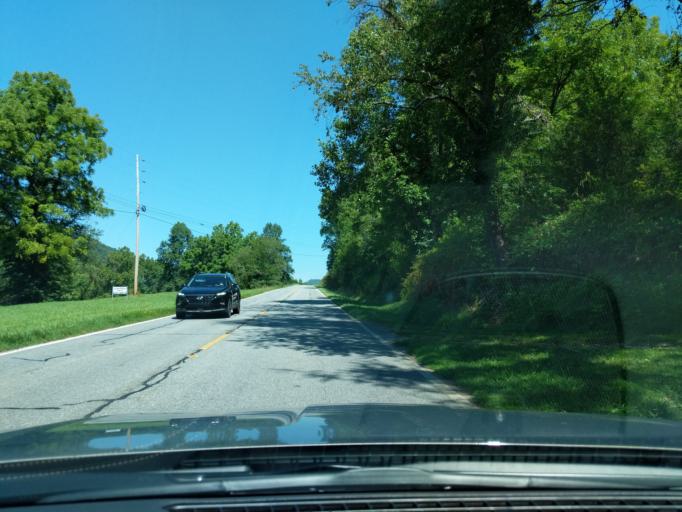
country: US
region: Georgia
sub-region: Towns County
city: Hiawassee
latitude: 34.8973
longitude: -83.7210
